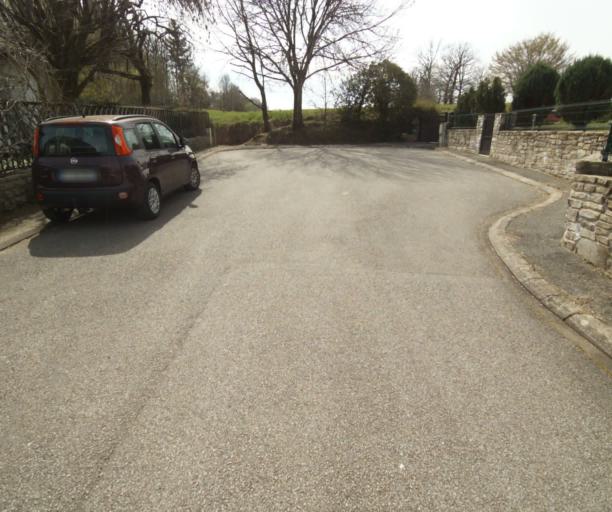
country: FR
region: Limousin
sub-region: Departement de la Correze
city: Naves
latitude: 45.3113
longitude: 1.7636
